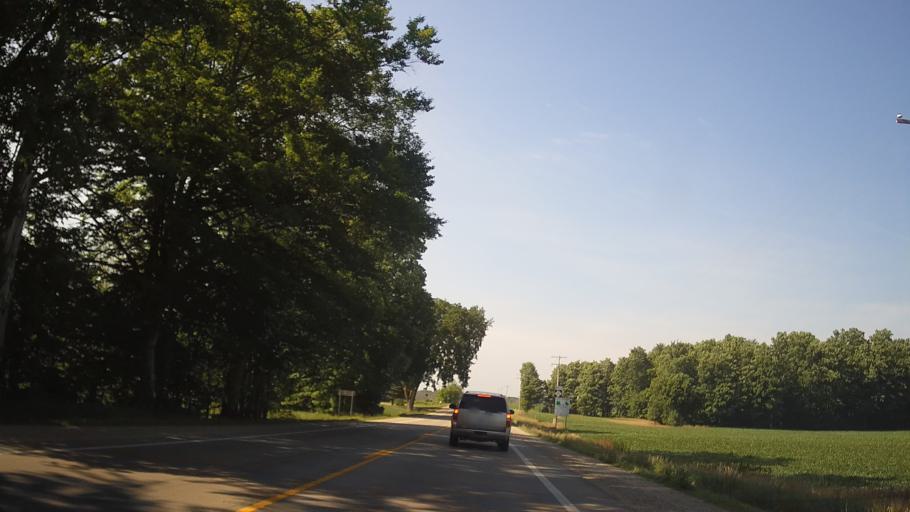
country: US
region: Michigan
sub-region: Ogemaw County
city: West Branch
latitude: 44.3139
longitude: -84.1257
